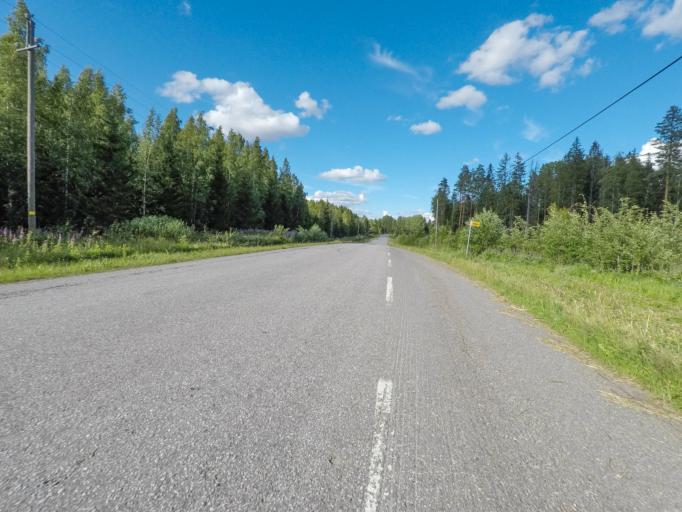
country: FI
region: South Karelia
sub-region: Imatra
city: Imatra
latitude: 61.1385
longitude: 28.7385
